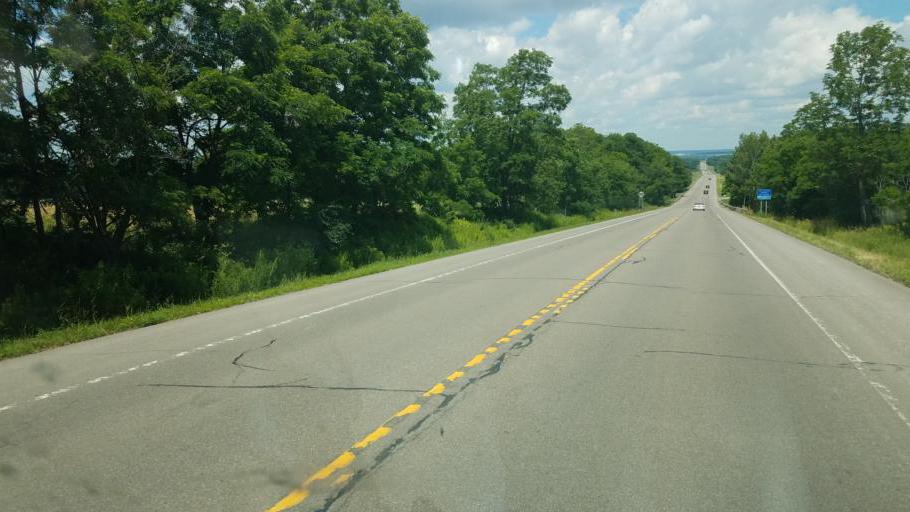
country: US
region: New York
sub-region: Yates County
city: Keuka Park
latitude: 42.5934
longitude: -77.0372
